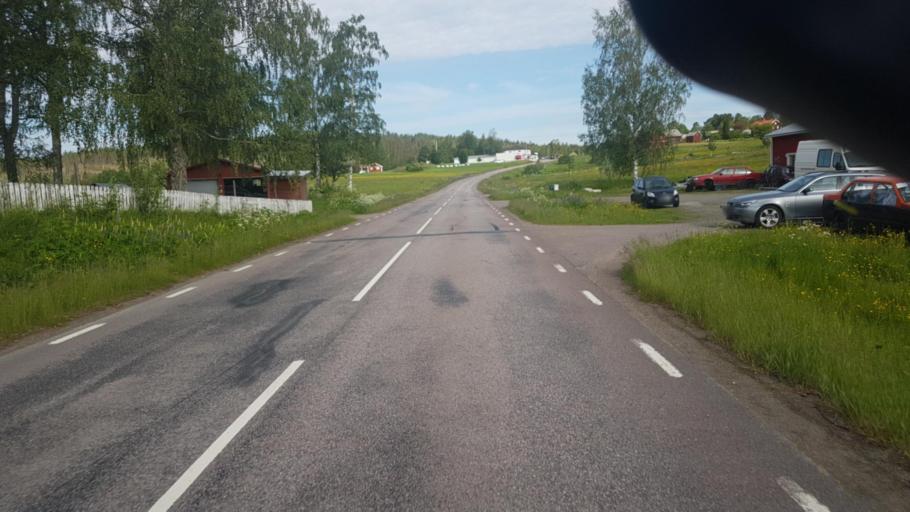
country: SE
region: Vaermland
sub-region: Arvika Kommun
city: Arvika
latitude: 59.7927
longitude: 12.6153
